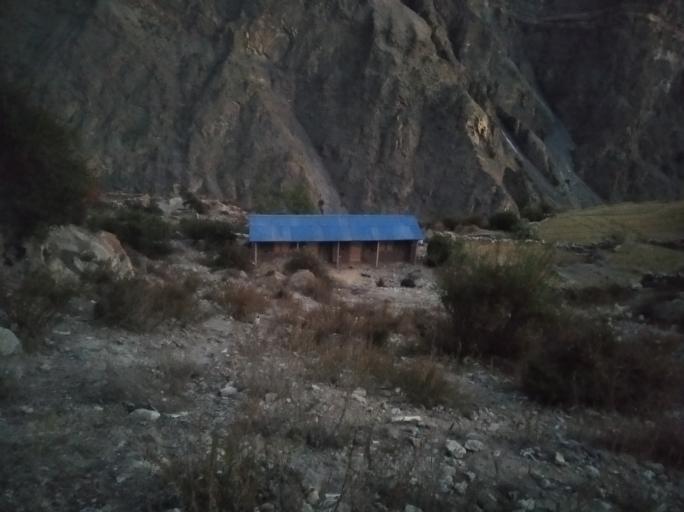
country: NP
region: Western Region
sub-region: Dhawalagiri Zone
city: Jomsom
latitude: 28.8734
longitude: 83.3552
